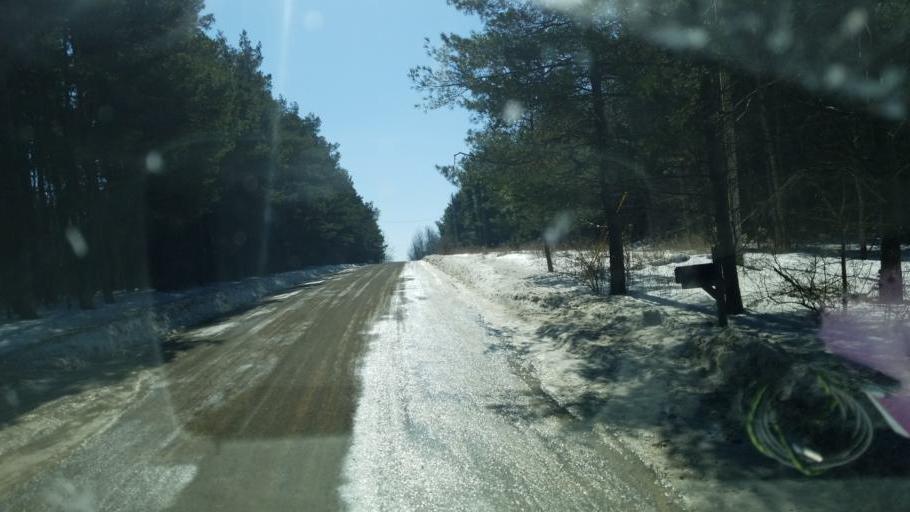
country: US
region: New York
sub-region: Allegany County
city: Alfred
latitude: 42.2553
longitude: -77.7316
